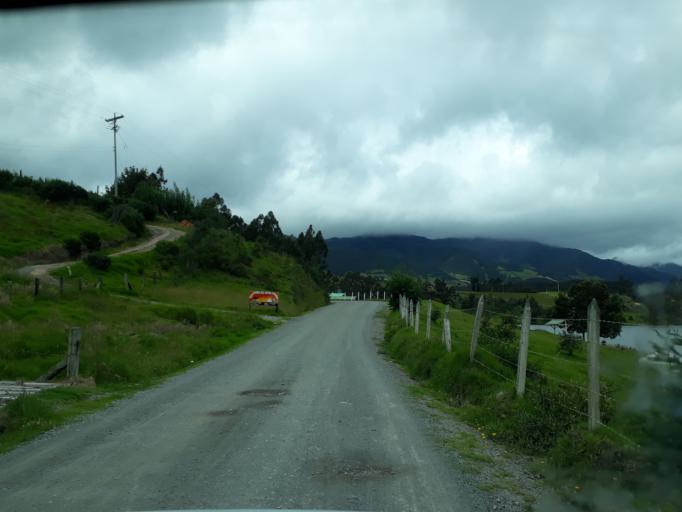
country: CO
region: Cundinamarca
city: La Mesa
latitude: 5.2937
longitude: -73.9063
